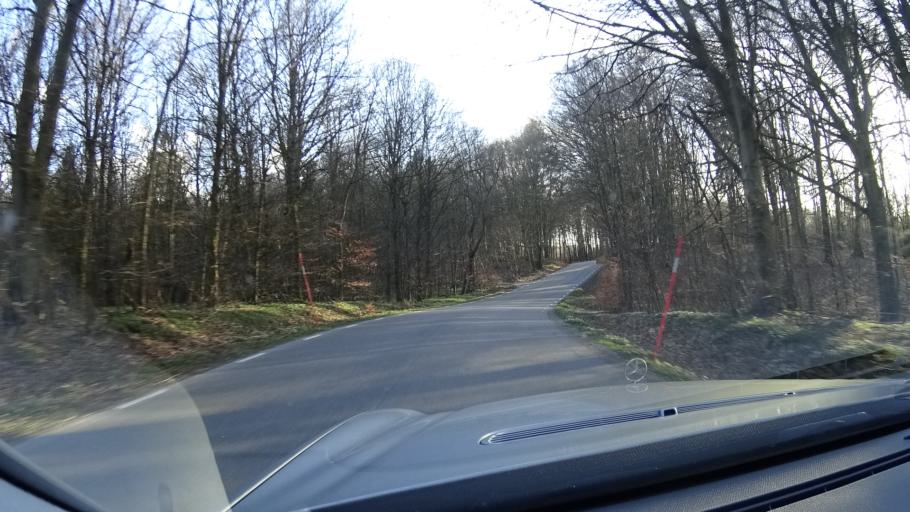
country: SE
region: Skane
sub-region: Hoors Kommun
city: Hoeoer
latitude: 55.9198
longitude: 13.5066
